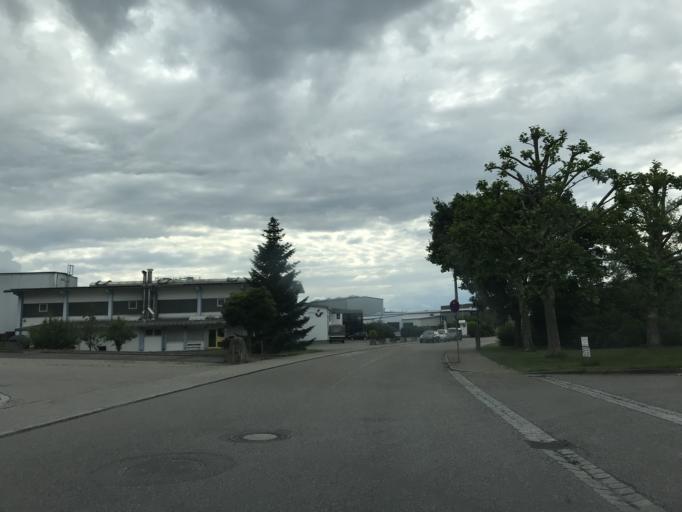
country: DE
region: Baden-Wuerttemberg
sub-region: Freiburg Region
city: Schopfheim
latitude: 47.6424
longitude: 7.8060
